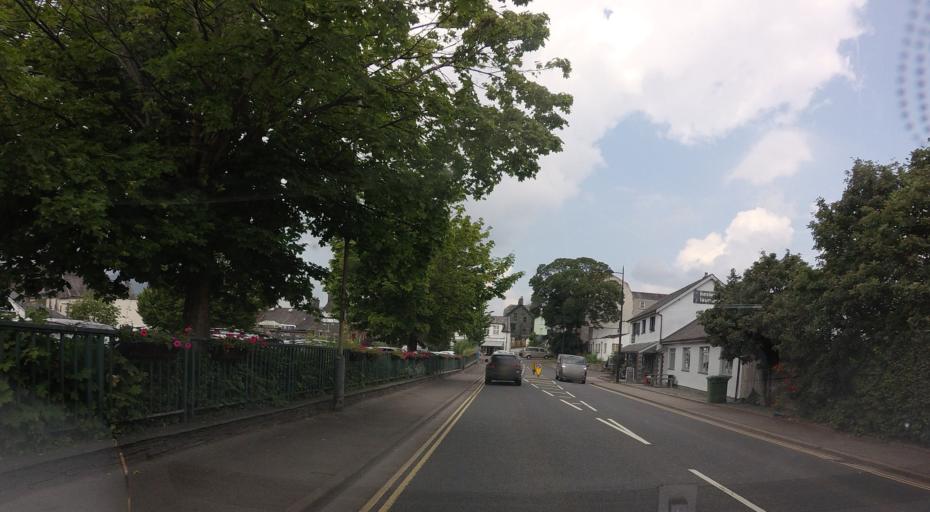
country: GB
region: England
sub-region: Cumbria
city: Keswick
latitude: 54.6018
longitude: -3.1364
